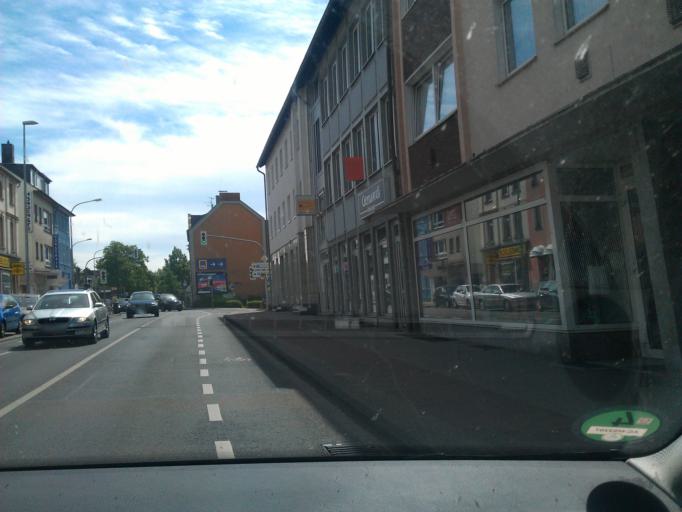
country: DE
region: North Rhine-Westphalia
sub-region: Regierungsbezirk Dusseldorf
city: Hilden
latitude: 51.1688
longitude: 6.9397
